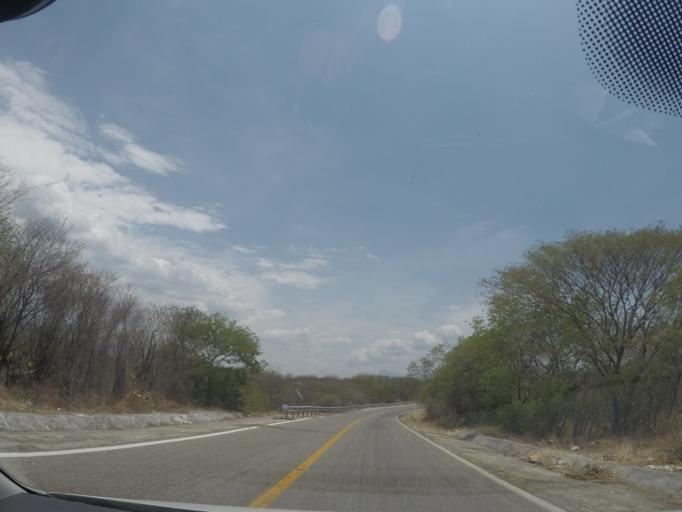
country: MX
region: Oaxaca
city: Magdalena Tequisistlan
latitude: 16.4100
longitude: -95.6256
